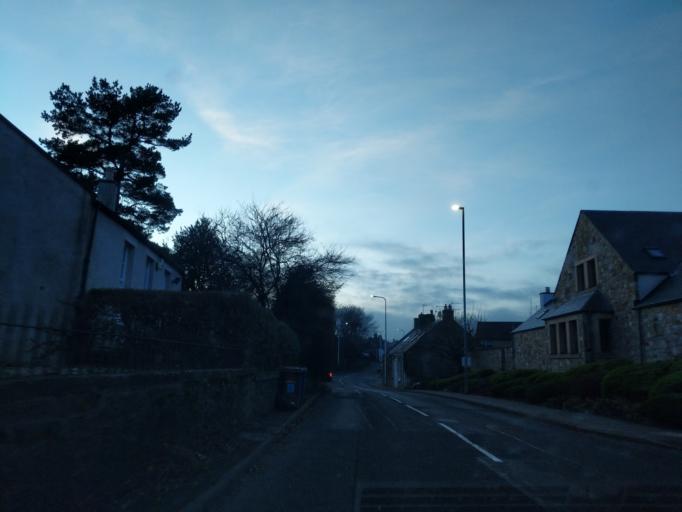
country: GB
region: Scotland
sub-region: Midlothian
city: Loanhead
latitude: 55.8781
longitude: -3.1406
